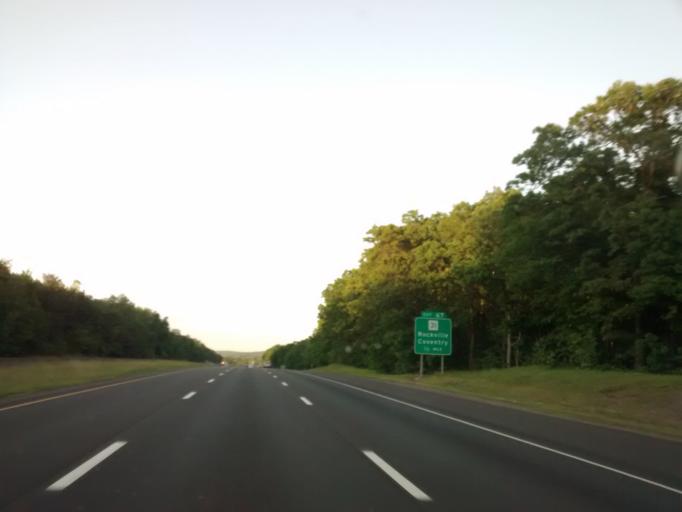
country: US
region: Connecticut
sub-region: Tolland County
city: Rockville
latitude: 41.8466
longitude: -72.4409
